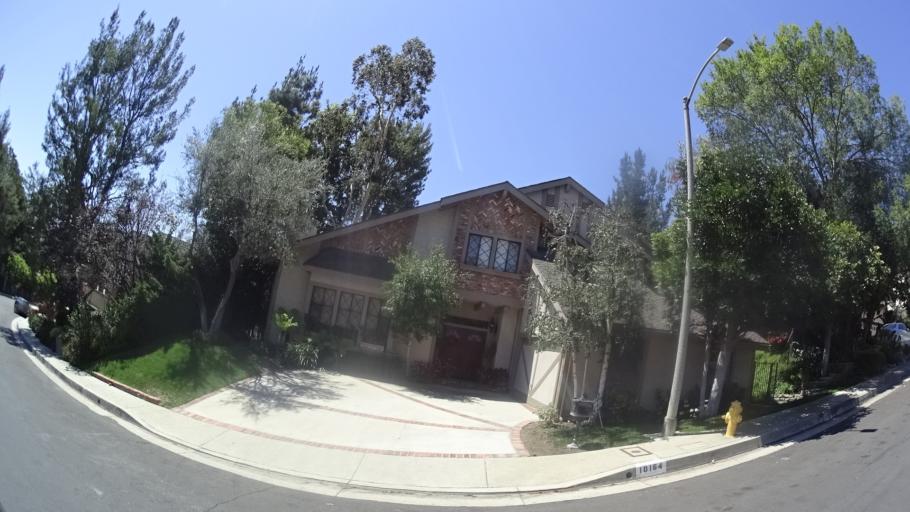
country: US
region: California
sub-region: Los Angeles County
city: Sherman Oaks
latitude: 34.1180
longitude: -118.4416
